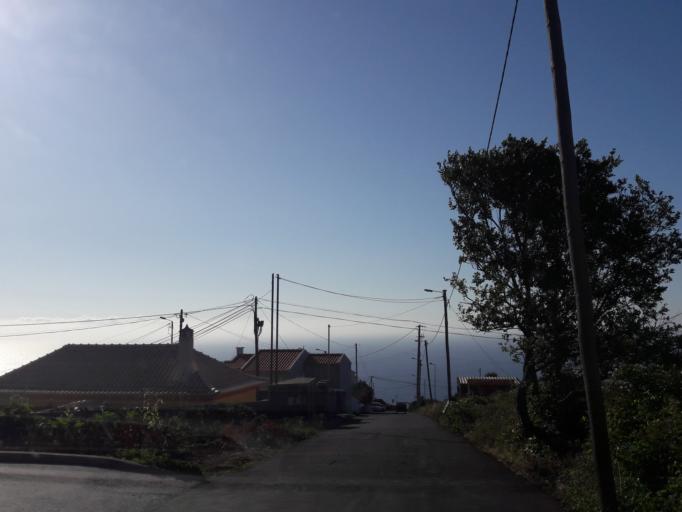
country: PT
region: Madeira
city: Canico
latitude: 32.6520
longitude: -16.8576
